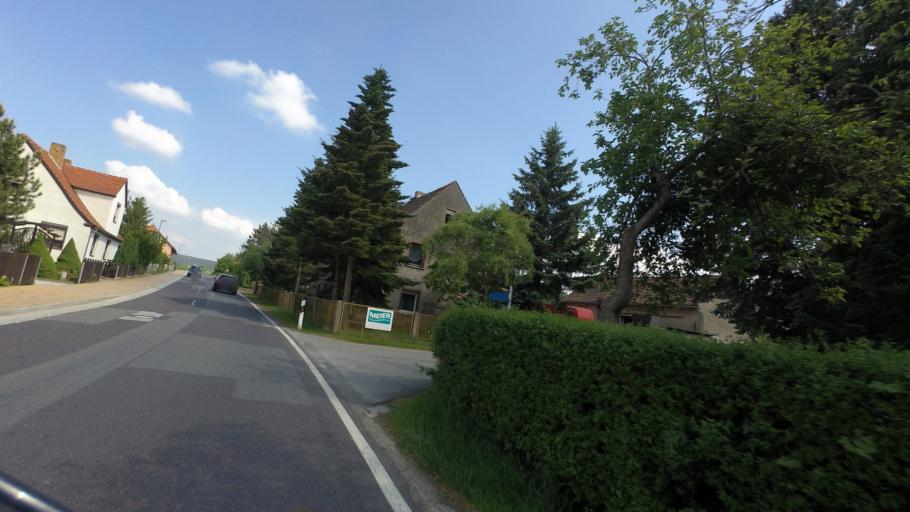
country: DE
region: Saxony
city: Weissenberg
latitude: 51.2581
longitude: 14.6475
